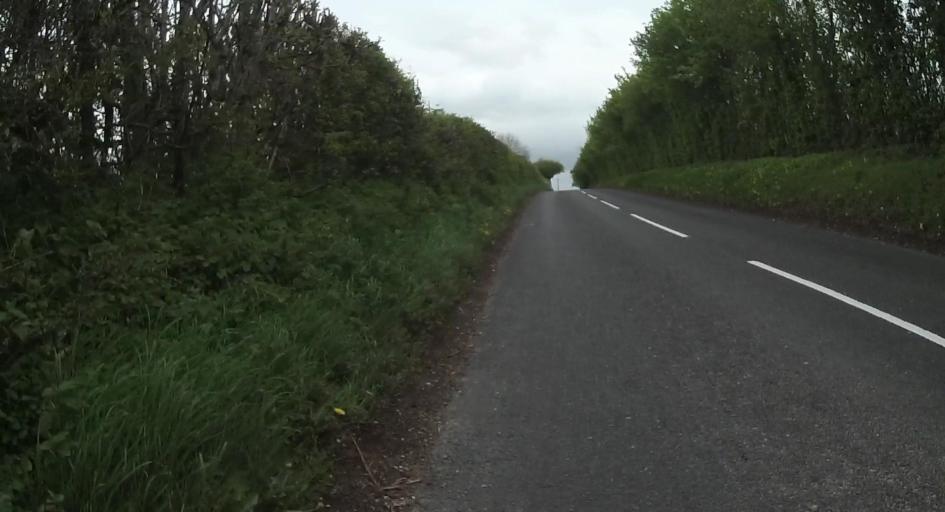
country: GB
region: England
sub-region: Hampshire
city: Colden Common
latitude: 51.0249
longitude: -1.2661
